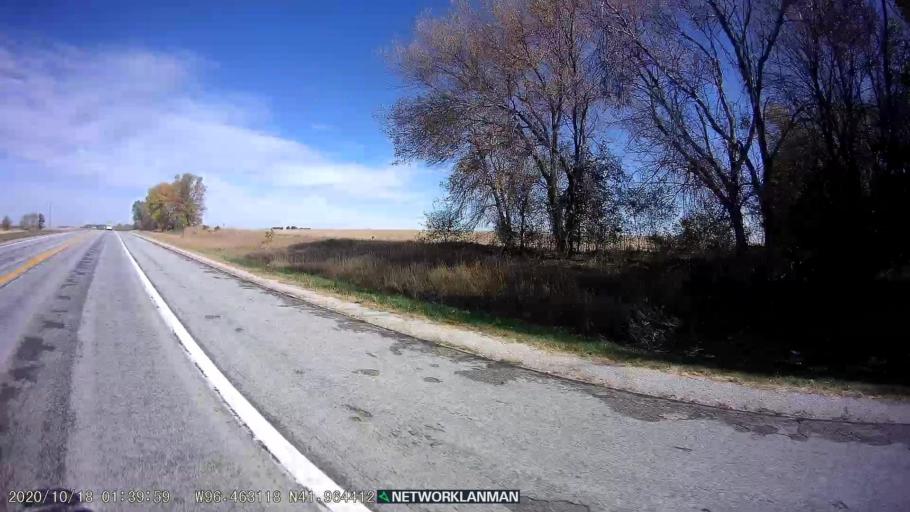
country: US
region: Nebraska
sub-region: Burt County
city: Oakland
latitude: 41.9645
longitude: -96.4629
